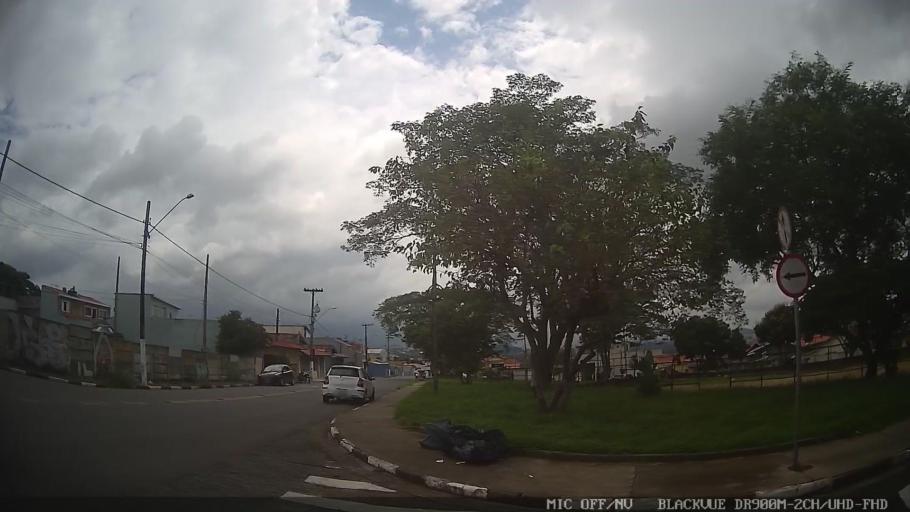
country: BR
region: Sao Paulo
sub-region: Atibaia
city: Atibaia
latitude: -23.1201
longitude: -46.5835
